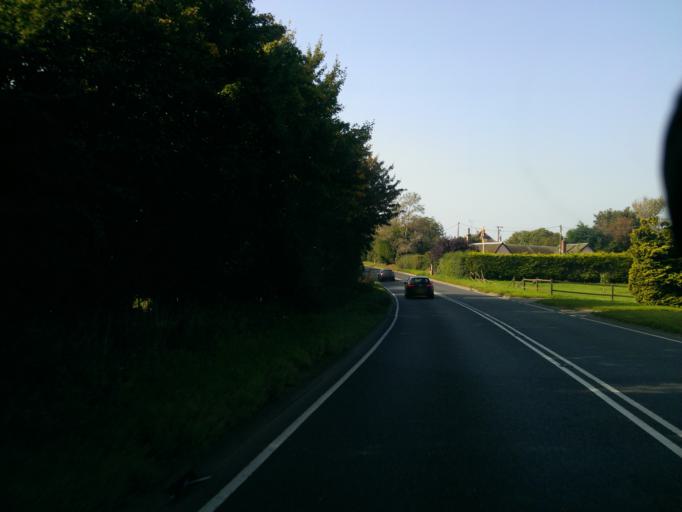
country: GB
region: England
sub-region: Essex
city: Layer de la Haye
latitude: 51.8674
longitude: 0.8485
